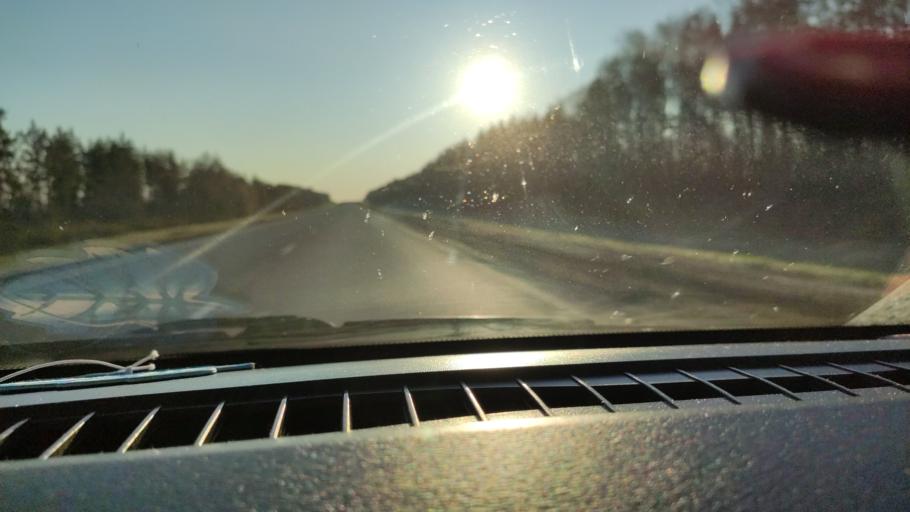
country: RU
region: Saratov
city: Sennoy
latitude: 52.1538
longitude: 47.0087
